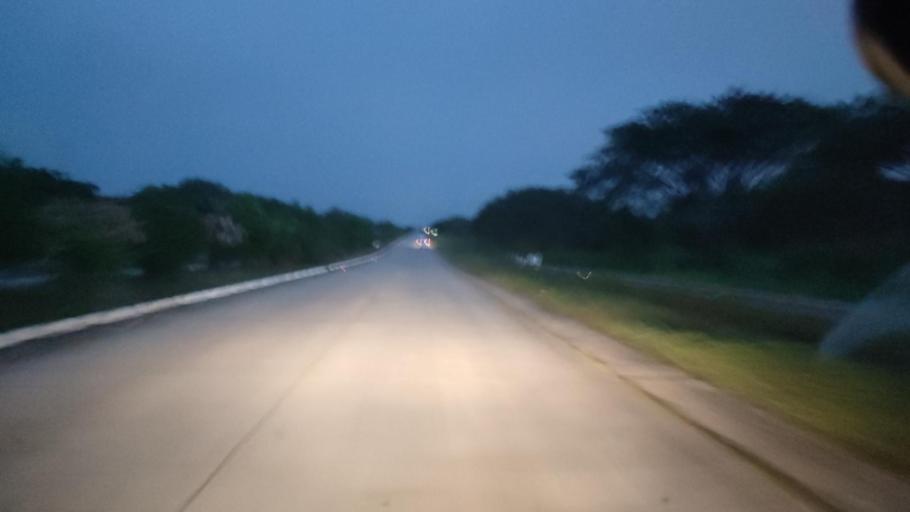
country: MM
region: Mandalay
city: Nay Pyi Taw
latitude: 19.9925
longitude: 95.9731
